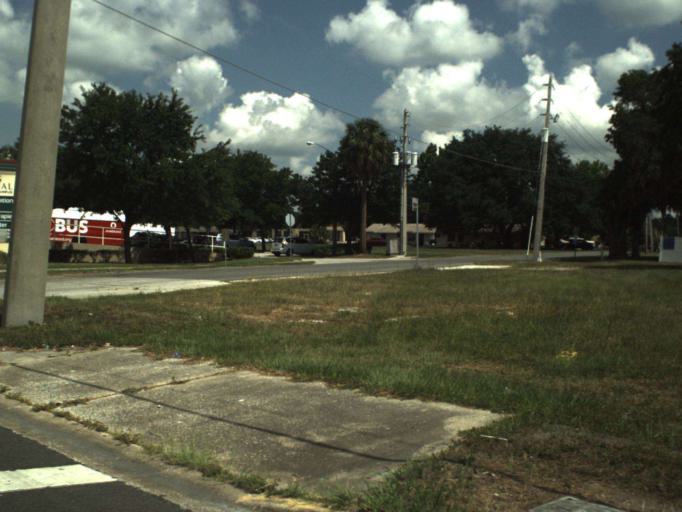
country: US
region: Florida
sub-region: Lake County
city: Leesburg
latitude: 28.8155
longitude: -81.8732
